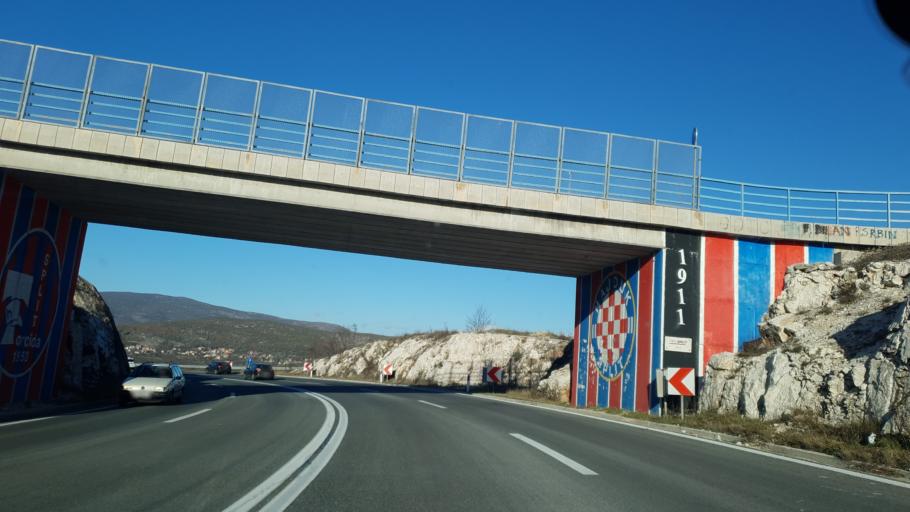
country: HR
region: Splitsko-Dalmatinska
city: Dugopolje
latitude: 43.6083
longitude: 16.6010
